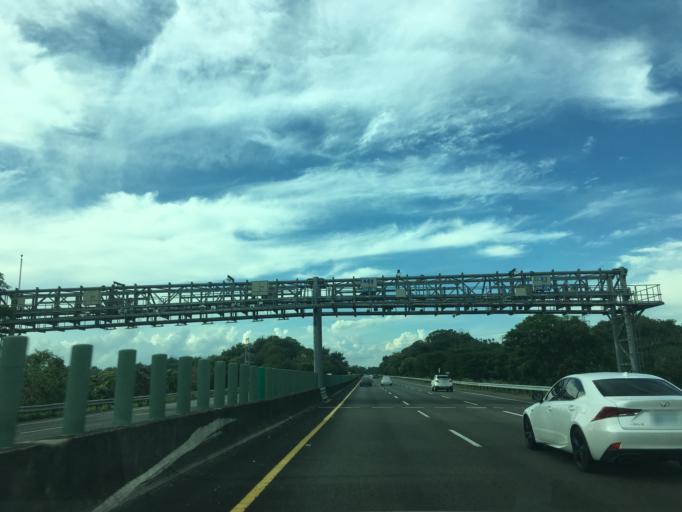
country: TW
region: Taiwan
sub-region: Chiayi
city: Jiayi Shi
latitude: 23.5574
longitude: 120.5050
